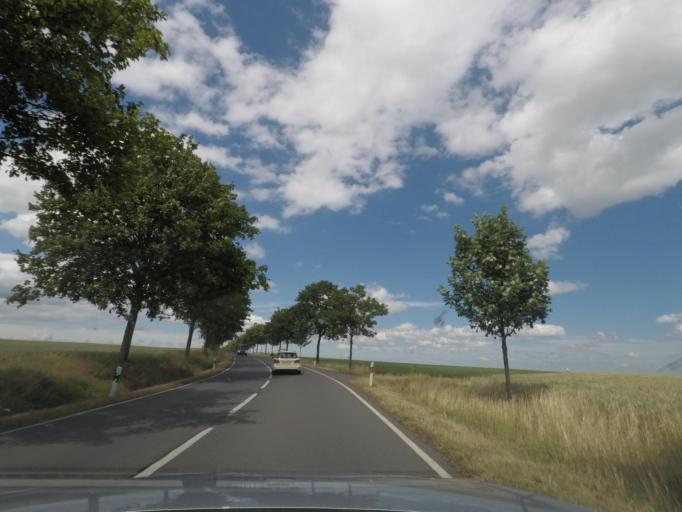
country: DE
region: Saxony-Anhalt
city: Gross Quenstedt
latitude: 51.9395
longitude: 11.1214
